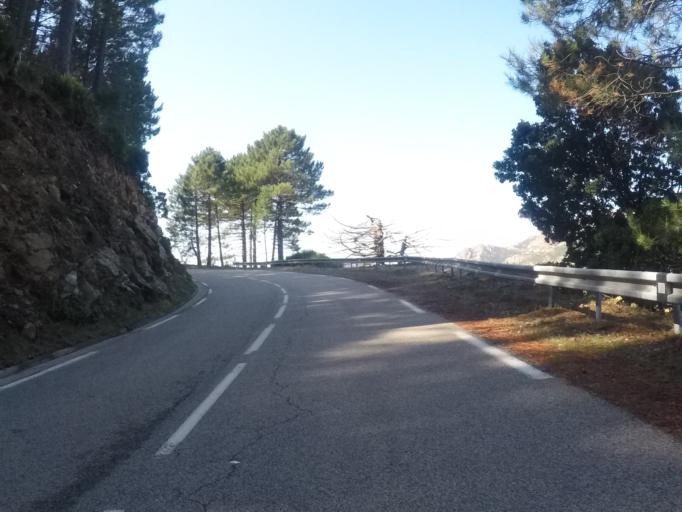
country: FR
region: Corsica
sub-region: Departement de la Corse-du-Sud
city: Zonza
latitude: 41.7740
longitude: 9.0751
